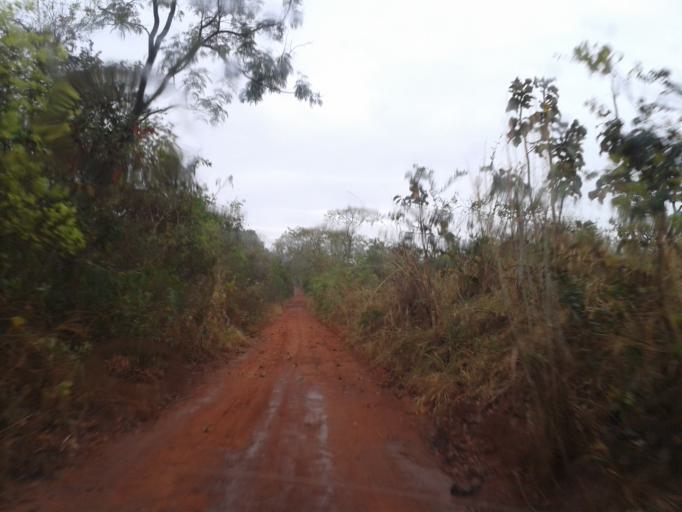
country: BR
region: Minas Gerais
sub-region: Campina Verde
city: Campina Verde
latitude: -19.3470
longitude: -49.5285
